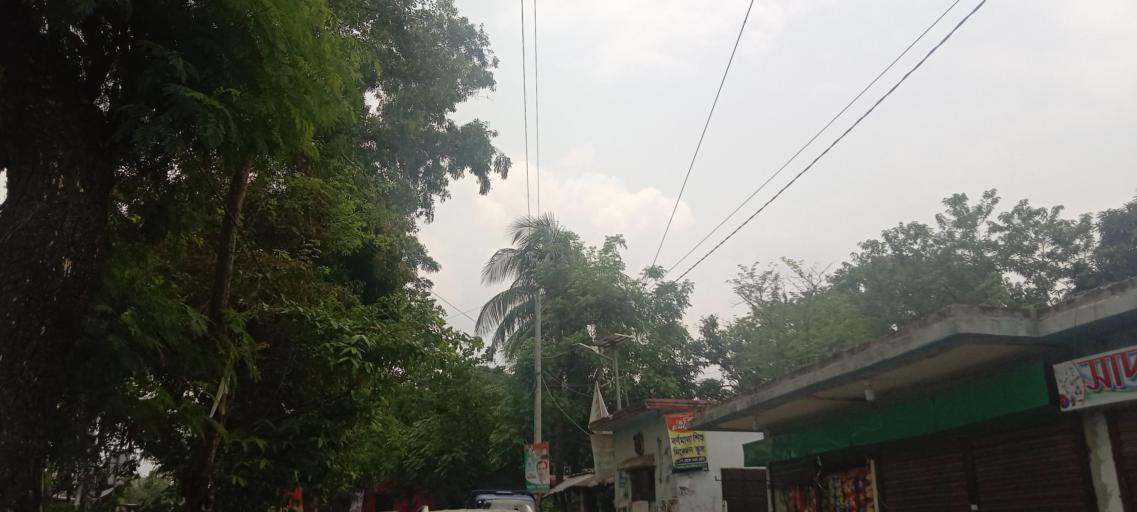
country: BD
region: Dhaka
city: Azimpur
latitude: 23.7116
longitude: 90.3457
